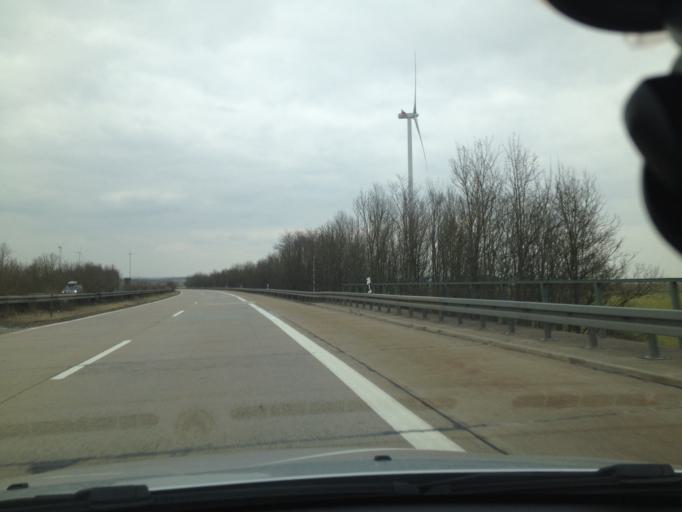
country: DE
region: Bavaria
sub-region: Regierungsbezirk Mittelfranken
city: Gollhofen
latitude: 49.5289
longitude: 10.1901
